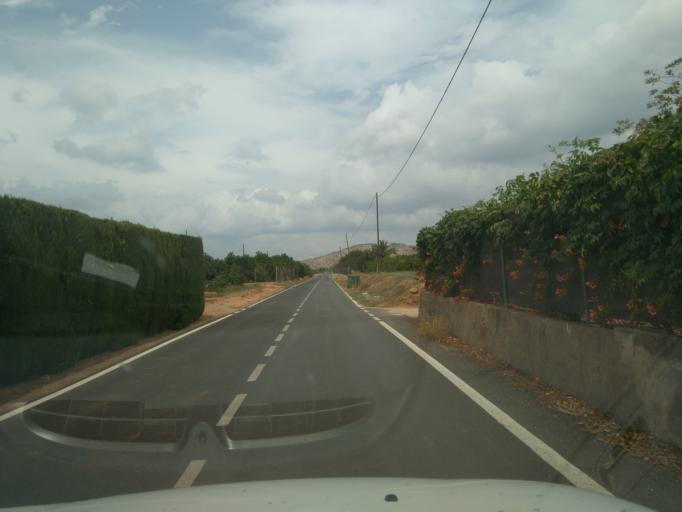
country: ES
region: Valencia
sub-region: Provincia de Valencia
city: Rafelguaraf
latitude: 39.0766
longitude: -0.4250
